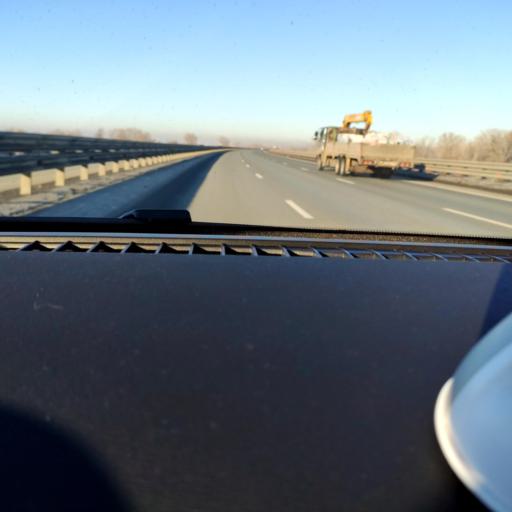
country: RU
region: Samara
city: Smyshlyayevka
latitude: 53.1629
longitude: 50.3240
